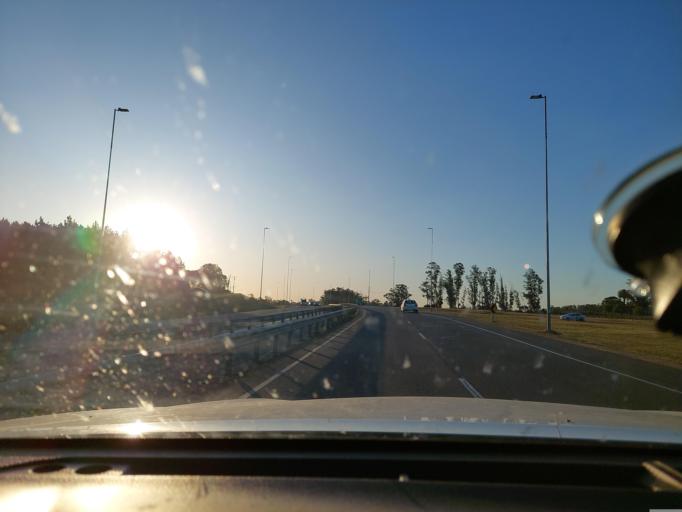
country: UY
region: Canelones
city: Empalme Olmos
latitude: -34.7005
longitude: -55.9147
